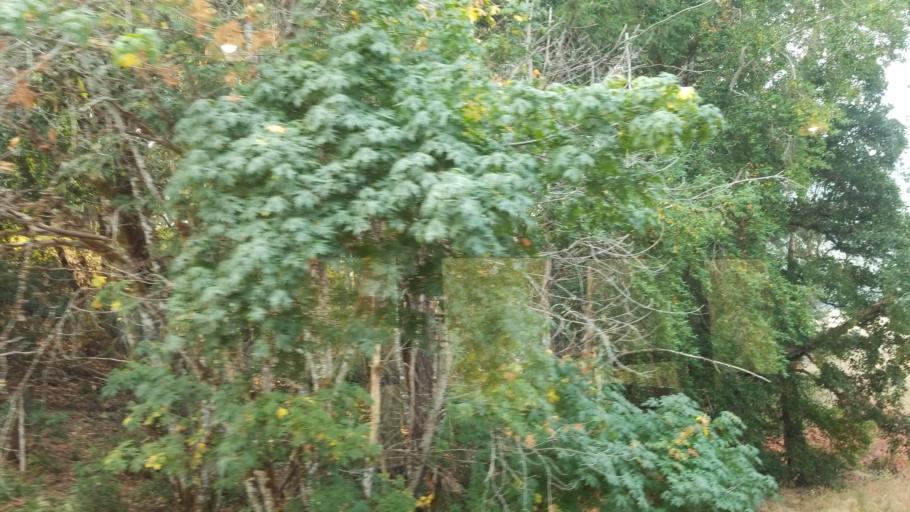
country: US
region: California
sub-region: Mendocino County
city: Willits
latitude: 39.4038
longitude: -123.3710
